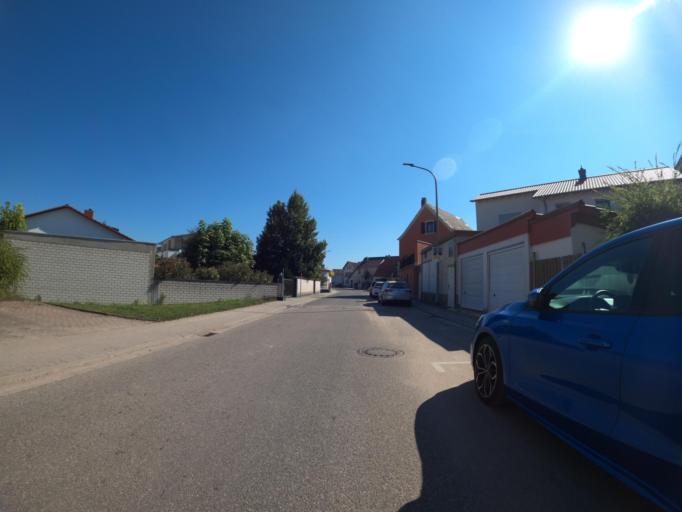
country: DE
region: Rheinland-Pfalz
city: Freinsheim
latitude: 49.5092
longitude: 8.2130
